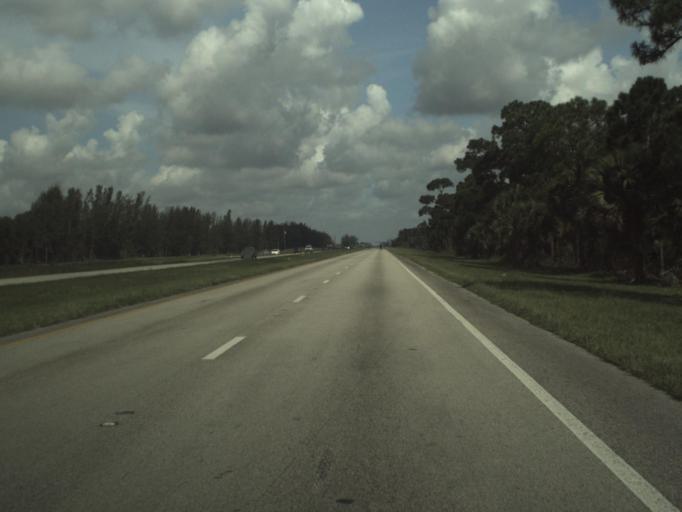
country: US
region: Florida
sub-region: Palm Beach County
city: Palm Beach Gardens
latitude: 26.8012
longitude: -80.1392
